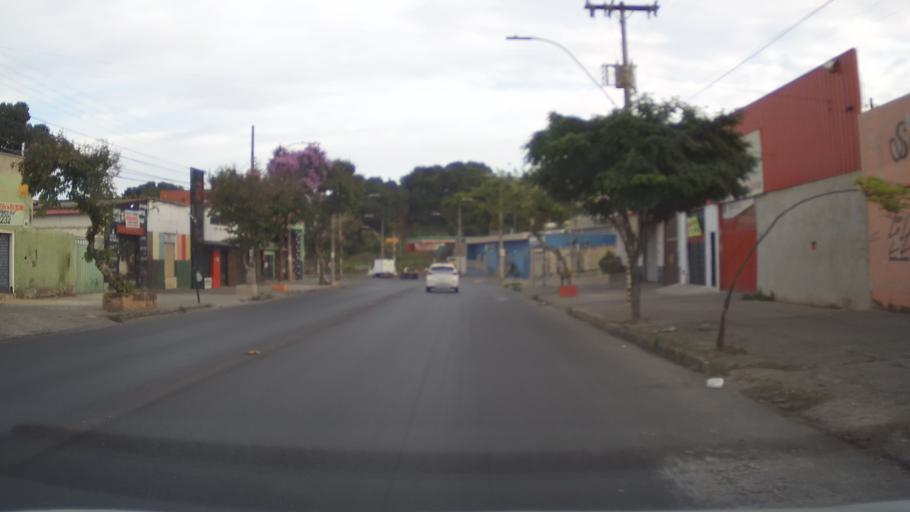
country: BR
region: Minas Gerais
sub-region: Contagem
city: Contagem
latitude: -19.9003
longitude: -44.0074
